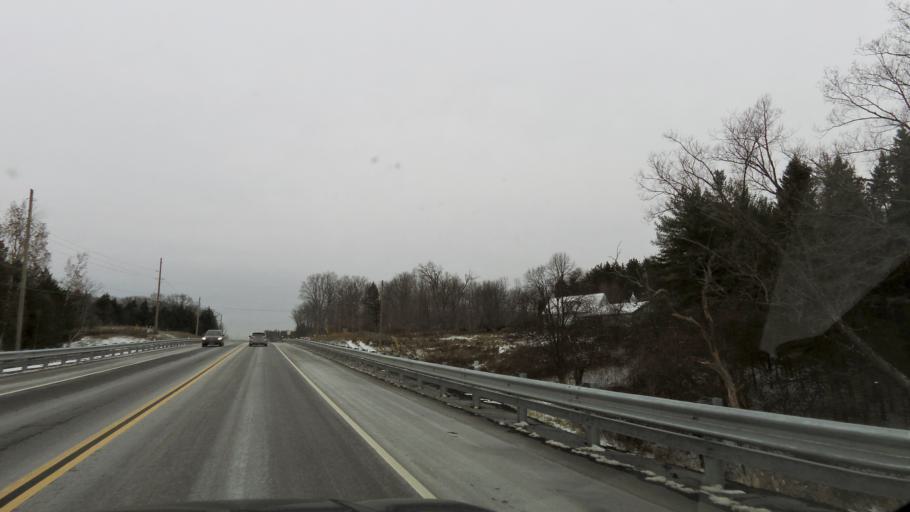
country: CA
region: Ontario
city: Newmarket
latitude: 44.0721
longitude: -79.5120
